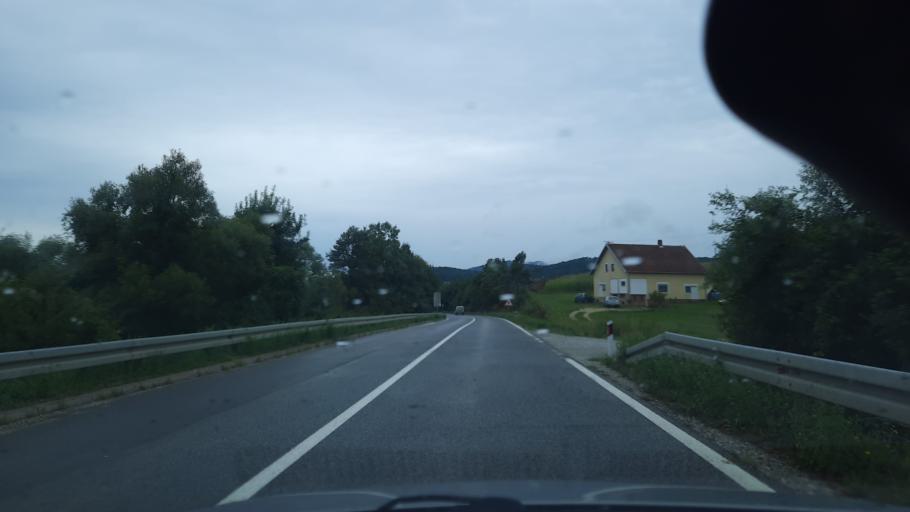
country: RS
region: Central Serbia
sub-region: Sumadijski Okrug
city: Knic
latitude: 43.8270
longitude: 20.7813
